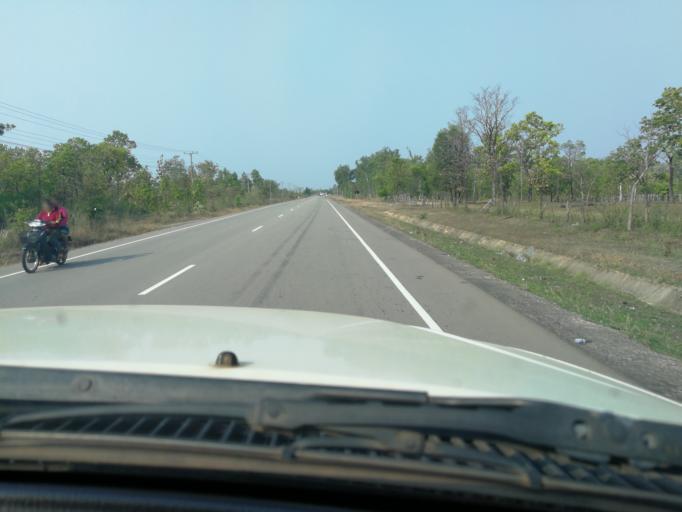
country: TH
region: Mukdahan
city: Wan Yai
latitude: 16.7073
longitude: 105.2380
